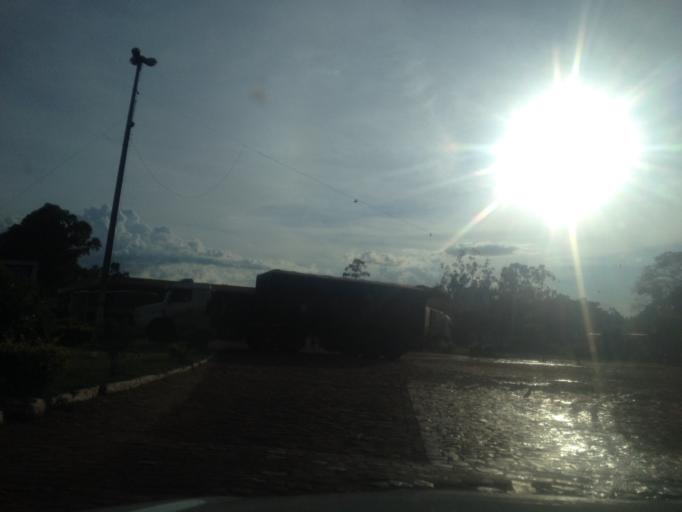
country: BR
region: Goias
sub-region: Jatai
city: Jatai
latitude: -17.9200
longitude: -51.6984
